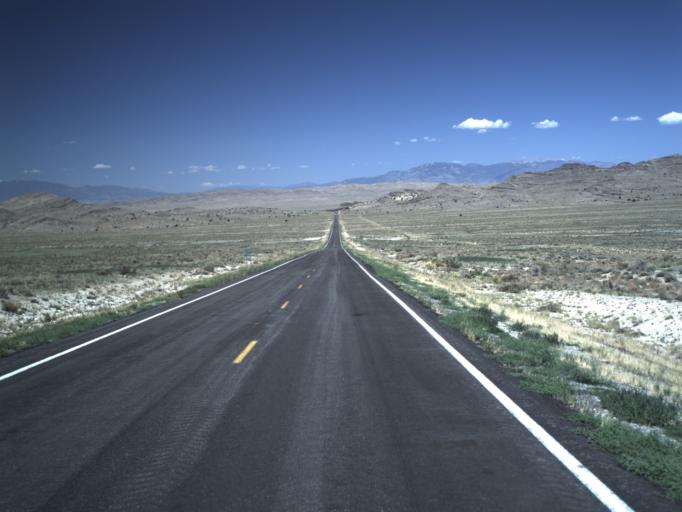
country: US
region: Utah
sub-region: Beaver County
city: Milford
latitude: 39.0739
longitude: -113.6700
